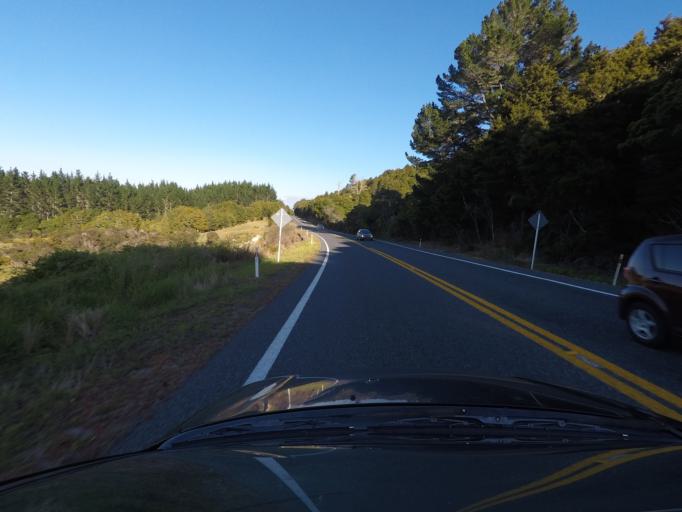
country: NZ
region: Northland
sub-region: Far North District
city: Kawakawa
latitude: -35.4802
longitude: 174.1180
